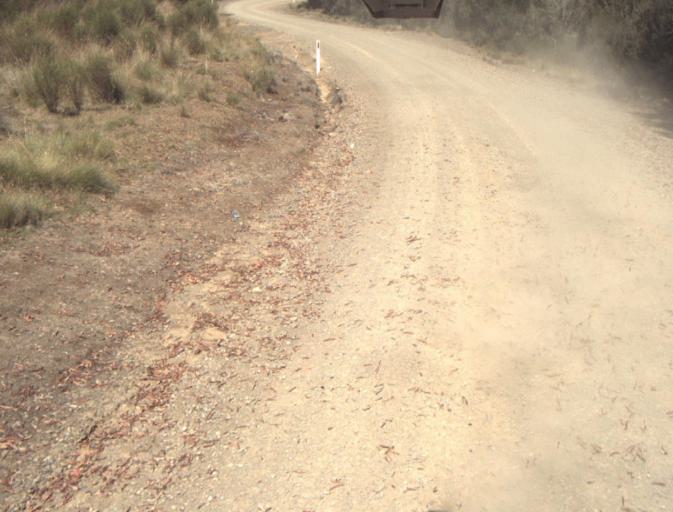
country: AU
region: Tasmania
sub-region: Dorset
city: Scottsdale
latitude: -41.3147
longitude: 147.4639
